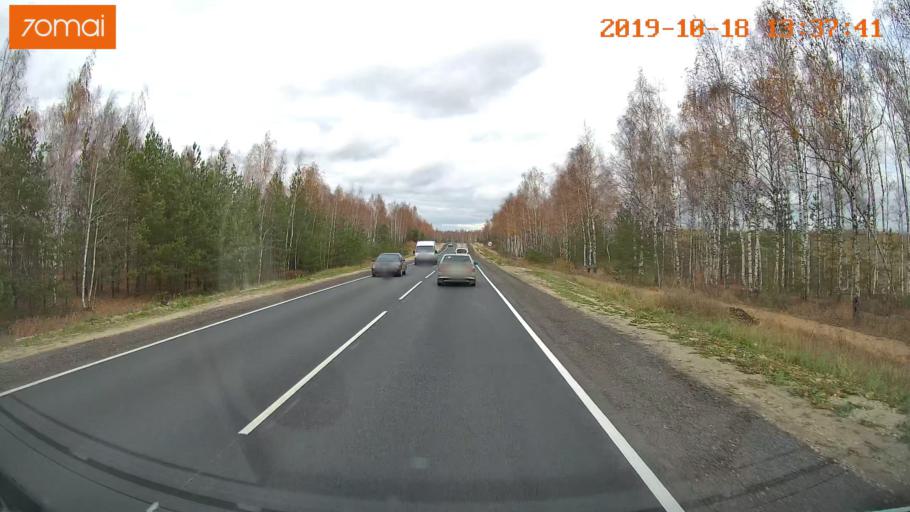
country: RU
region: Rjazan
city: Solotcha
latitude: 54.8817
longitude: 39.9977
